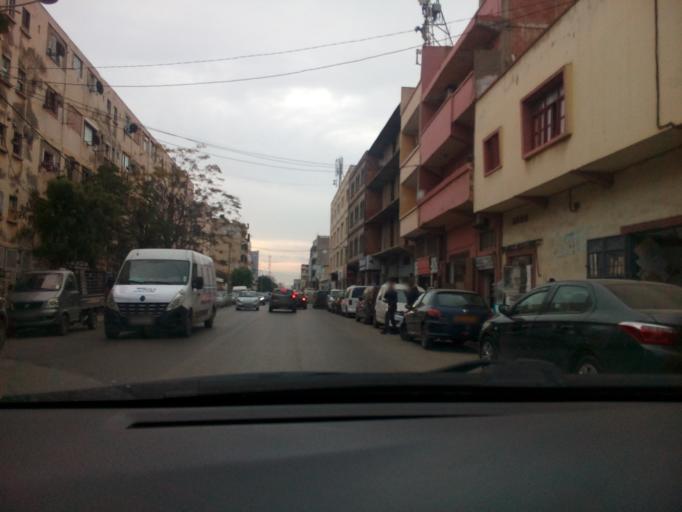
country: DZ
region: Oran
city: Oran
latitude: 35.6872
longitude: -0.6417
